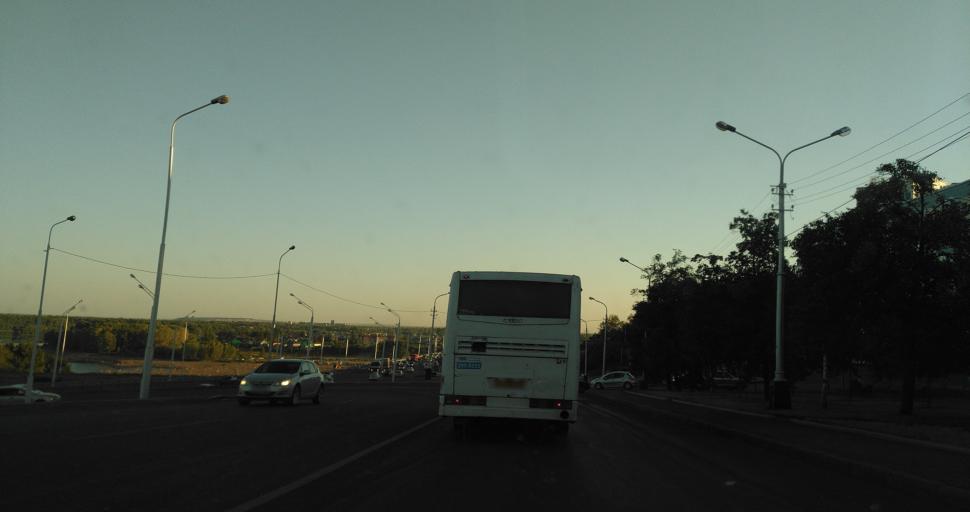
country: RU
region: Bashkortostan
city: Ufa
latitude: 54.7144
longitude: 55.9571
